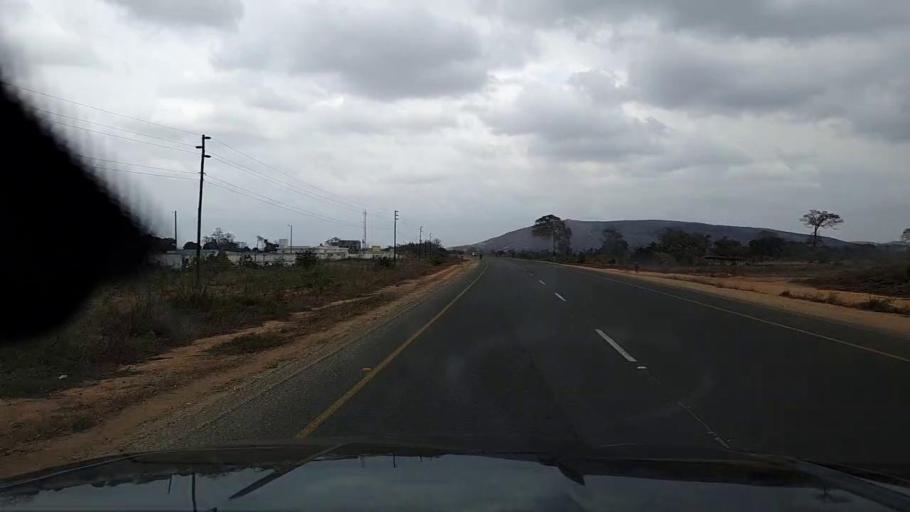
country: MZ
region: Nampula
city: Nampula
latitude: -15.1615
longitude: 39.3067
